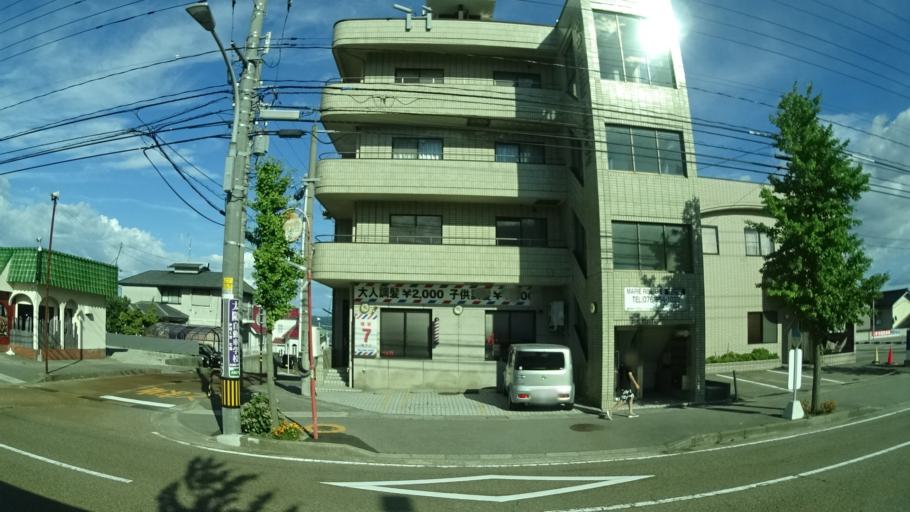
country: JP
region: Ishikawa
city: Kanazawa-shi
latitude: 36.6553
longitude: 136.6473
